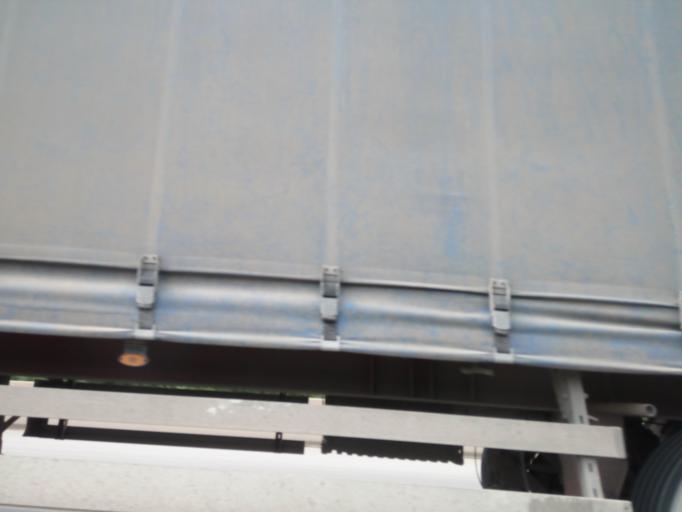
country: DZ
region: Tipaza
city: Mouzaia
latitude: 36.4496
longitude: 2.6865
